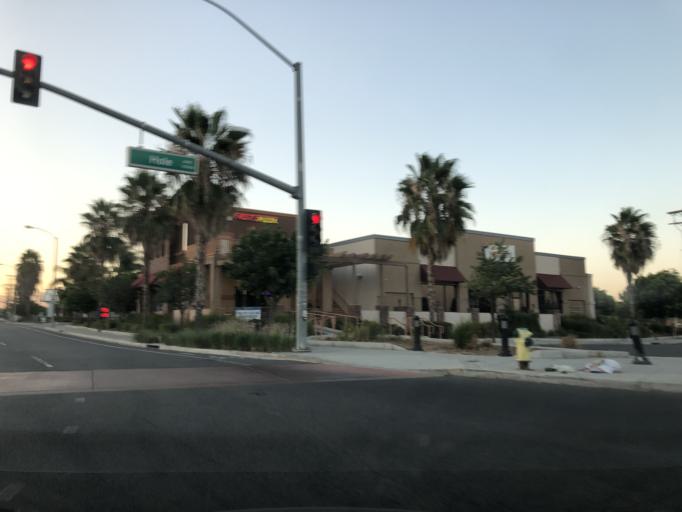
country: US
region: California
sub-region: Riverside County
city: Home Gardens
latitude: 33.9192
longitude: -117.4887
